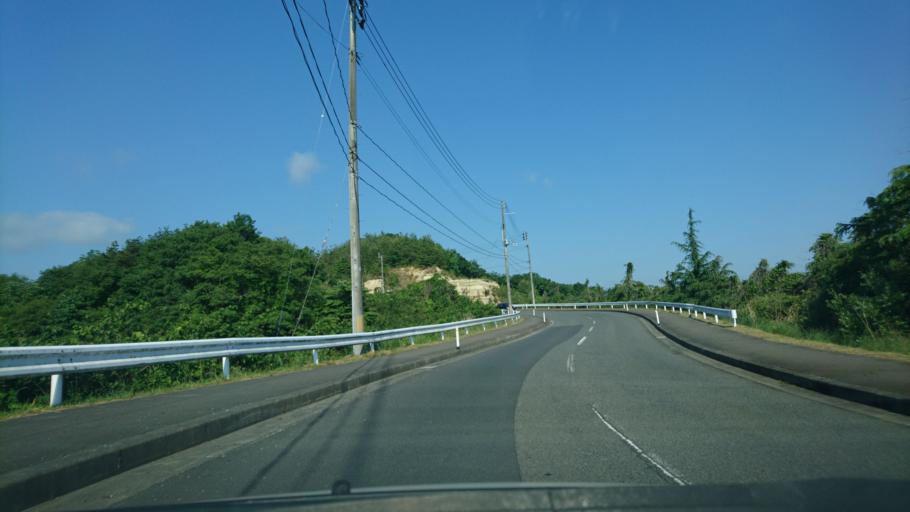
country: JP
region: Iwate
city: Ichinoseki
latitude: 38.9065
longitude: 141.1455
